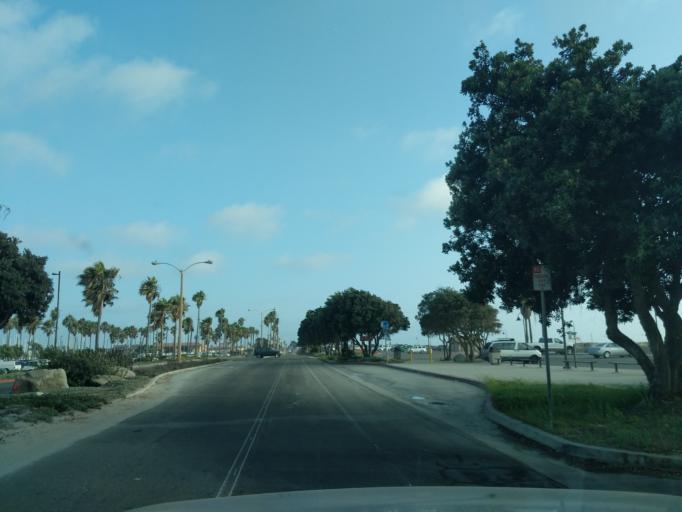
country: US
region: California
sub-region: Ventura County
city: Ventura
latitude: 34.2475
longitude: -119.2669
